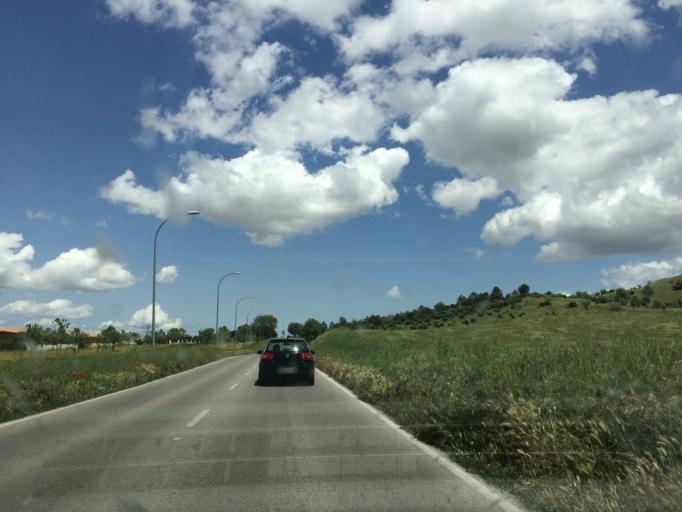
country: ES
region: Madrid
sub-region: Provincia de Madrid
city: Valdeolmos
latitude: 40.6922
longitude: -3.4482
